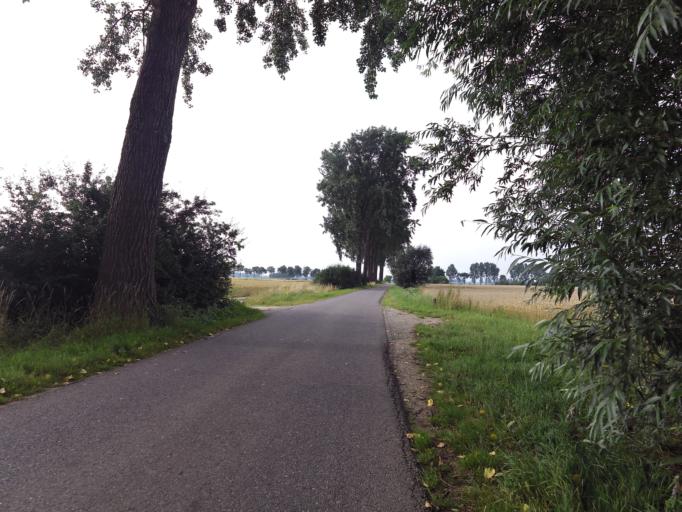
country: NL
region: Gelderland
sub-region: Gemeente Zevenaar
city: Zevenaar
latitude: 51.9643
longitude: 6.0762
